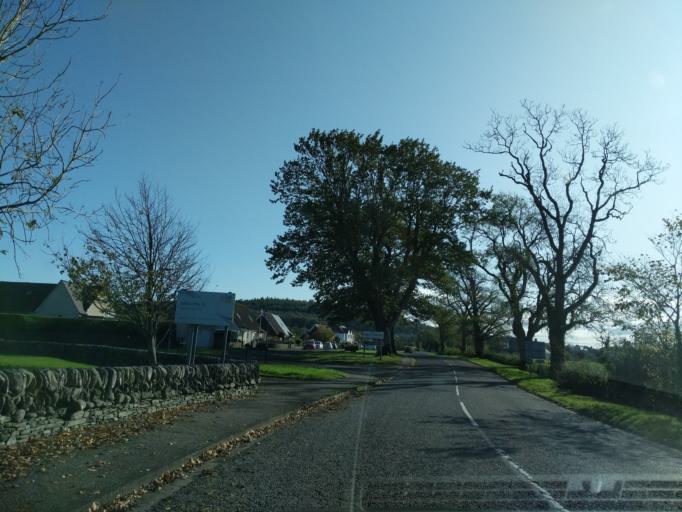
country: GB
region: Scotland
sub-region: Dumfries and Galloway
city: Kirkcudbright
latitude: 54.8426
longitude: -4.0547
